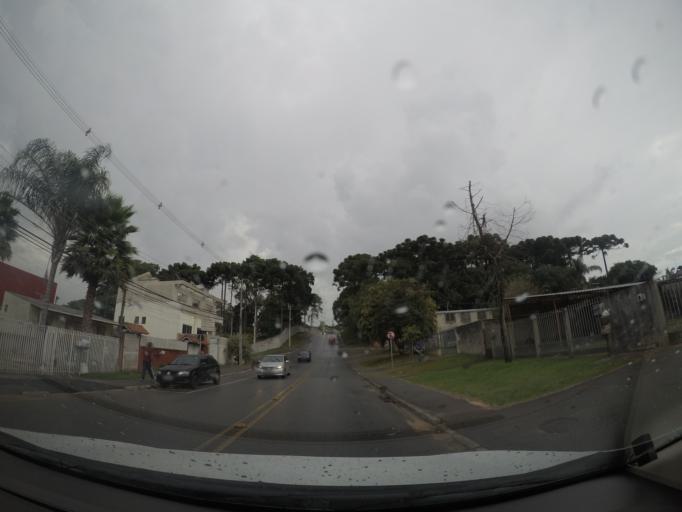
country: BR
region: Parana
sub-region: Sao Jose Dos Pinhais
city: Sao Jose dos Pinhais
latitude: -25.5173
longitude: -49.2504
